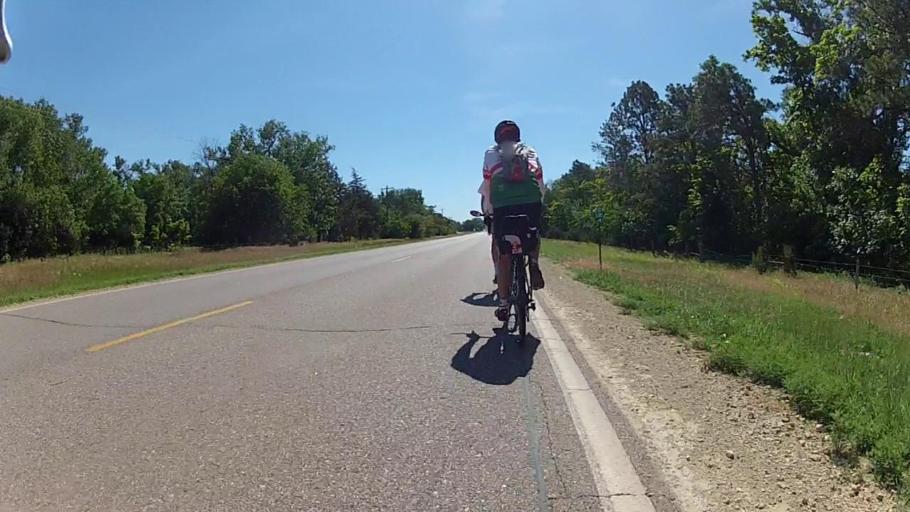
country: US
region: Kansas
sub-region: Barber County
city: Medicine Lodge
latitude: 37.2752
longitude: -98.6026
